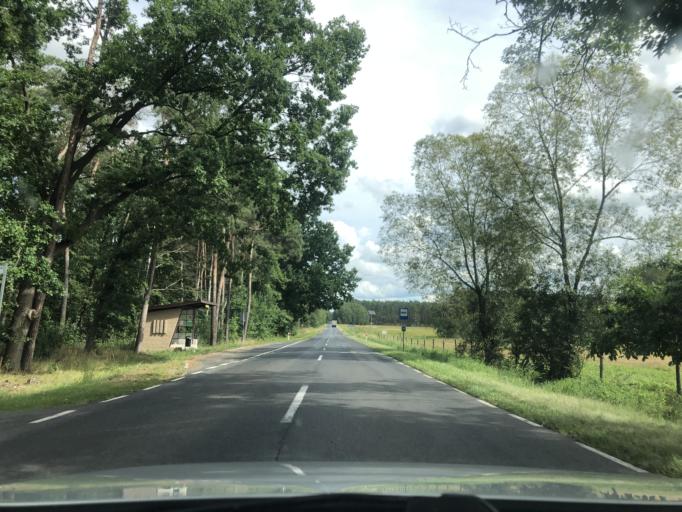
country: PL
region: Greater Poland Voivodeship
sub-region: Powiat czarnkowsko-trzcianecki
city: Trzcianka
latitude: 53.0692
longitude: 16.5571
